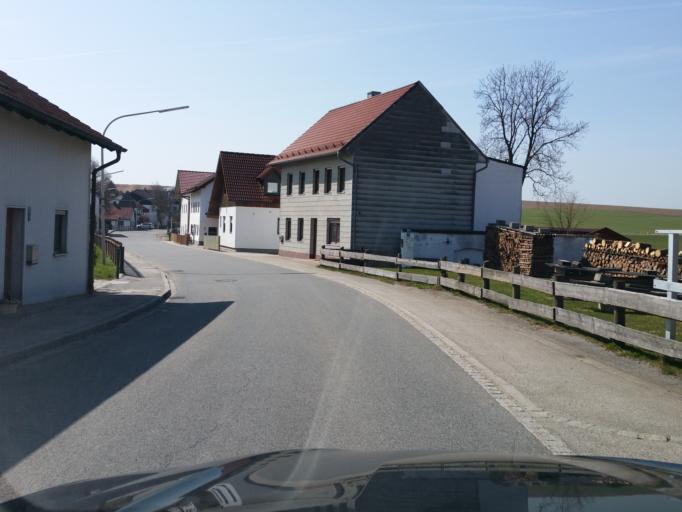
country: DE
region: Bavaria
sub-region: Lower Bavaria
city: Altfraunhofen
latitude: 48.4524
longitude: 12.1463
